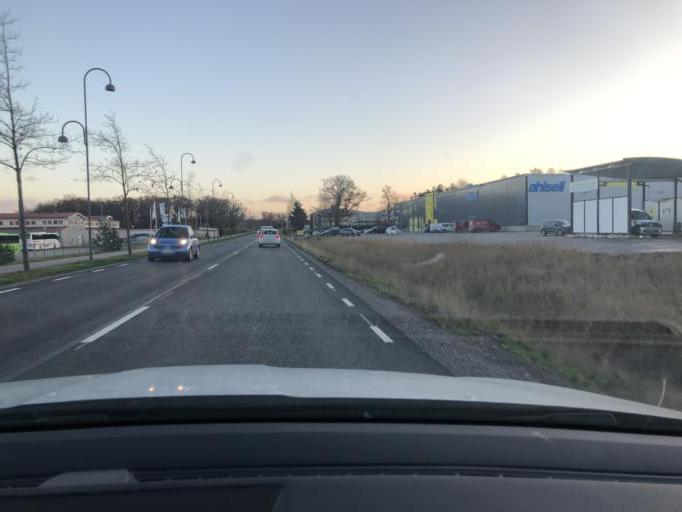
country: SE
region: Soedermanland
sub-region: Strangnas Kommun
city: Strangnas
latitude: 59.3519
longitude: 17.0298
